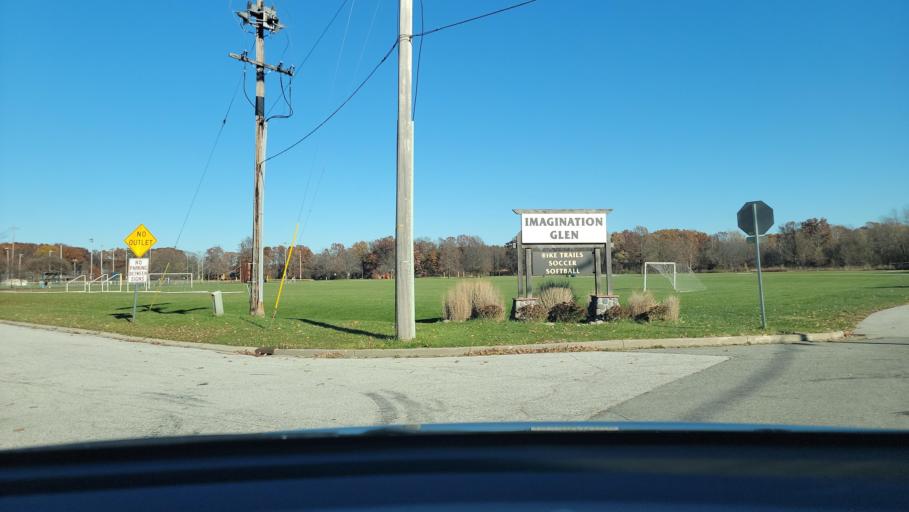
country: US
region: Indiana
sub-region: Porter County
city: Portage
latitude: 41.5866
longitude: -87.1440
